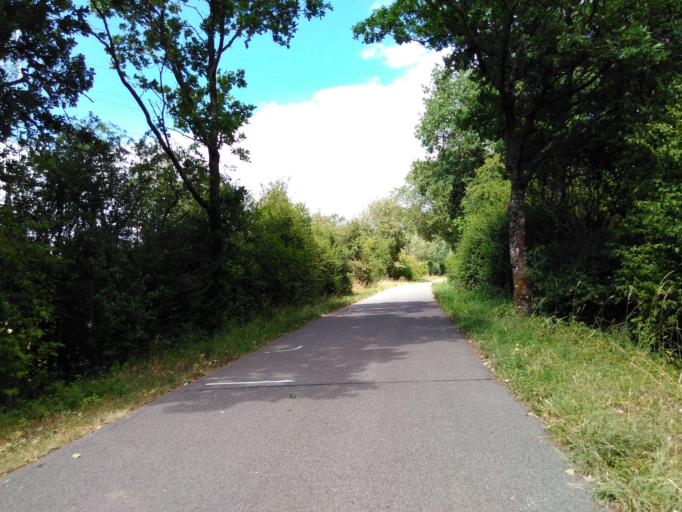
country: LU
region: Luxembourg
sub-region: Canton d'Esch-sur-Alzette
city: Petange
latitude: 49.5708
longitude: 5.8809
